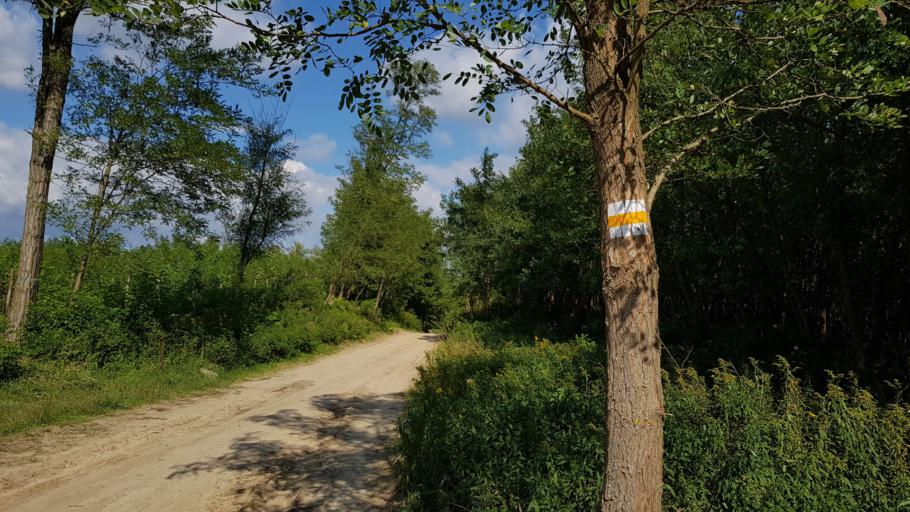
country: HU
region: Somogy
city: Nagybajom
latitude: 46.5167
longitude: 17.5292
